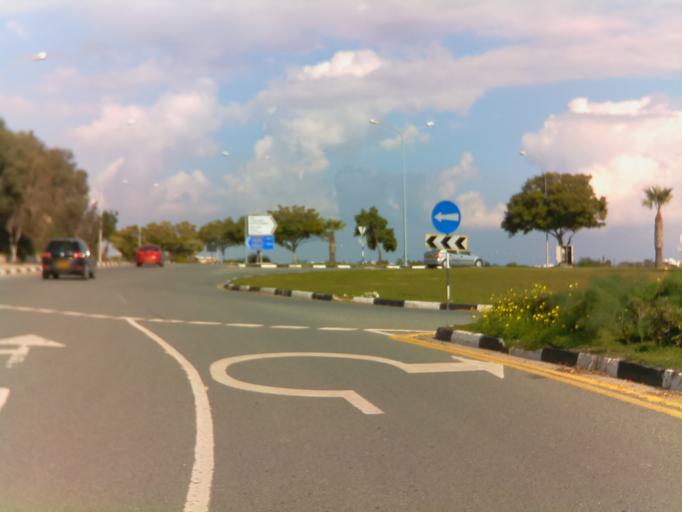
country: CY
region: Larnaka
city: Meneou
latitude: 34.8833
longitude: 33.6219
